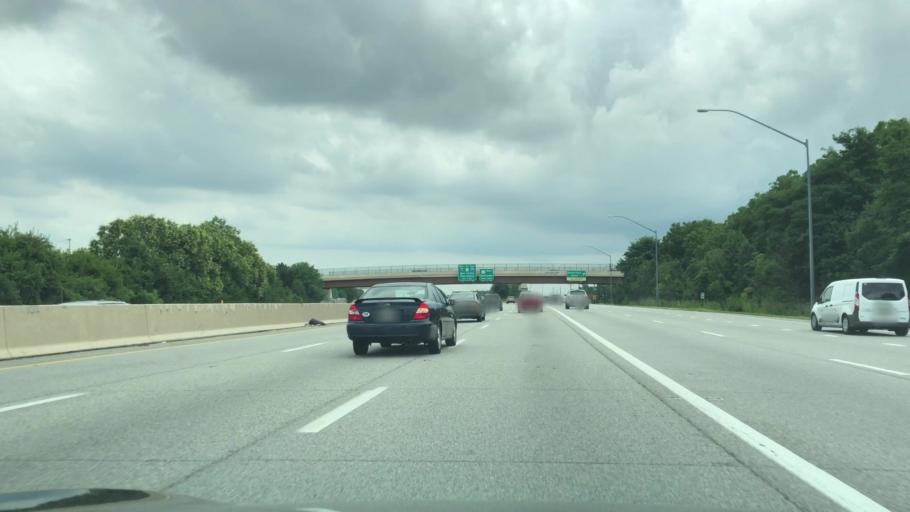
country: US
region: Pennsylvania
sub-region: Montgomery County
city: King of Prussia
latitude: 40.0767
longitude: -75.4137
